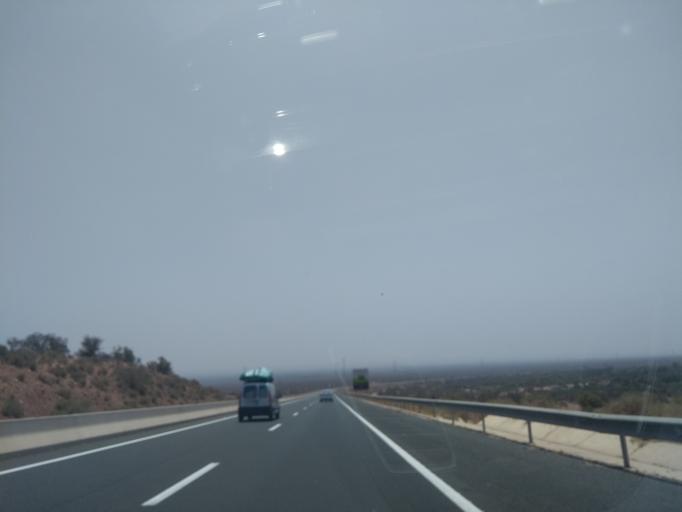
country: MA
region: Souss-Massa-Draa
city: Oulad Teima
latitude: 30.5366
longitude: -9.3211
